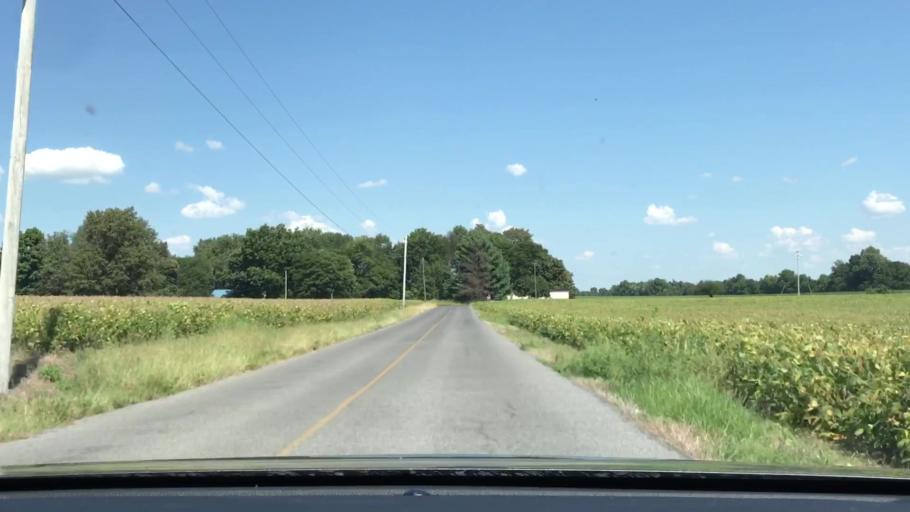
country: US
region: Kentucky
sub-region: Fulton County
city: Fulton
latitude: 36.5208
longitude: -88.9014
